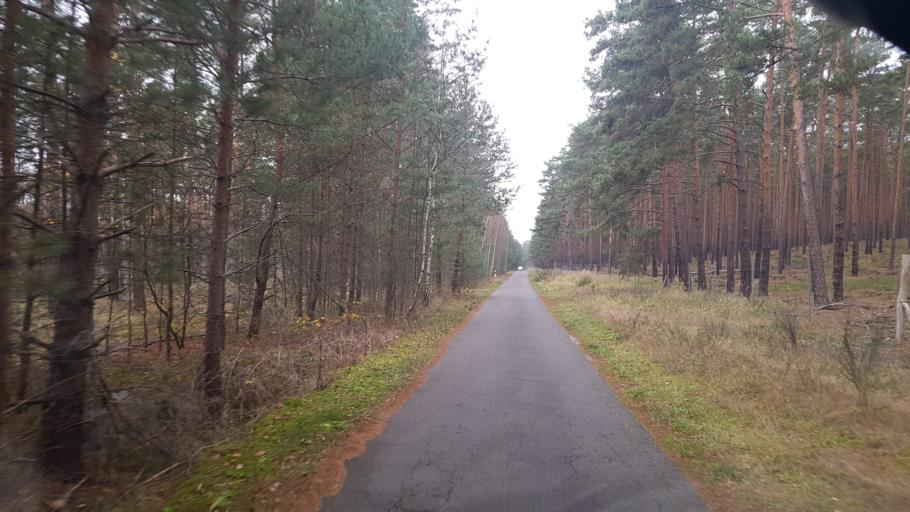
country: DE
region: Brandenburg
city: Schenkendobern
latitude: 51.9740
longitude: 14.6454
